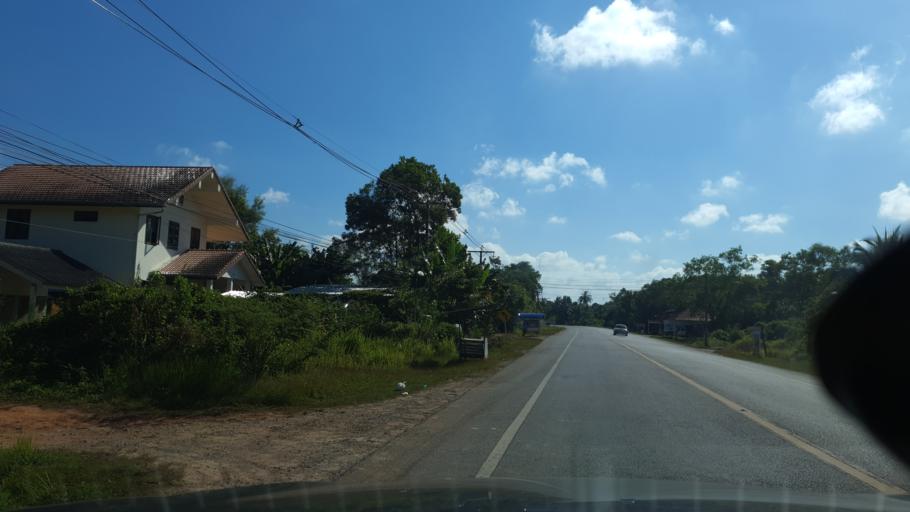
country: TH
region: Krabi
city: Krabi
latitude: 8.0274
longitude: 98.8733
